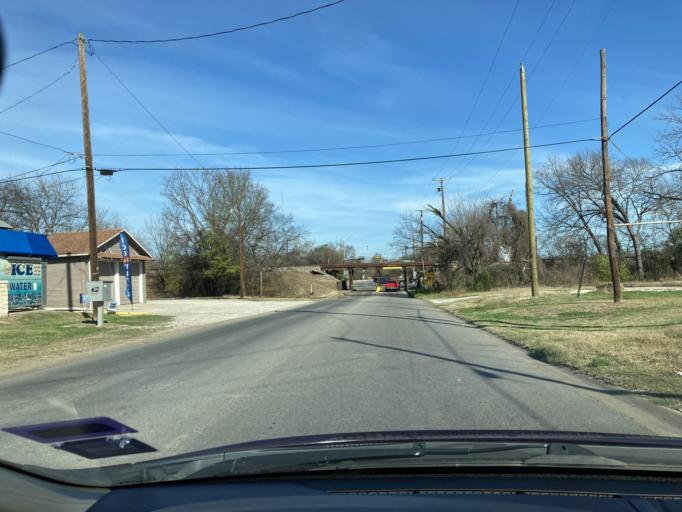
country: US
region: Texas
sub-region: Navarro County
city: Corsicana
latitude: 32.0993
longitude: -96.4644
